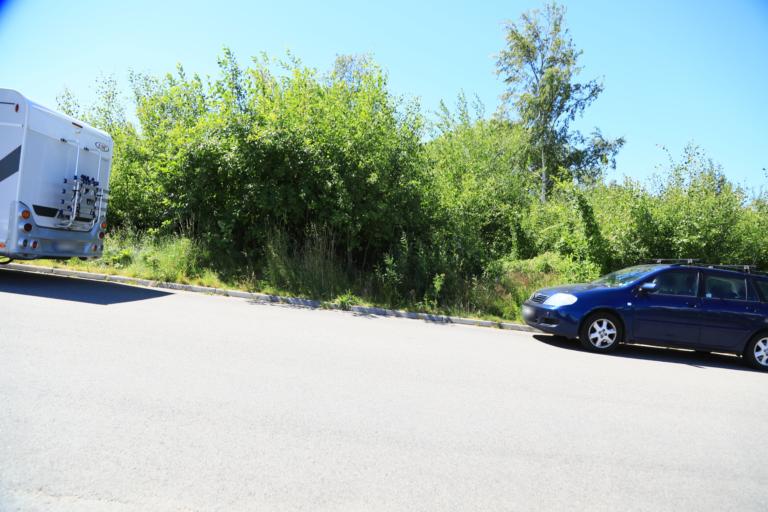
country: SE
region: Halland
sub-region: Varbergs Kommun
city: Traslovslage
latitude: 57.0888
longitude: 12.2767
